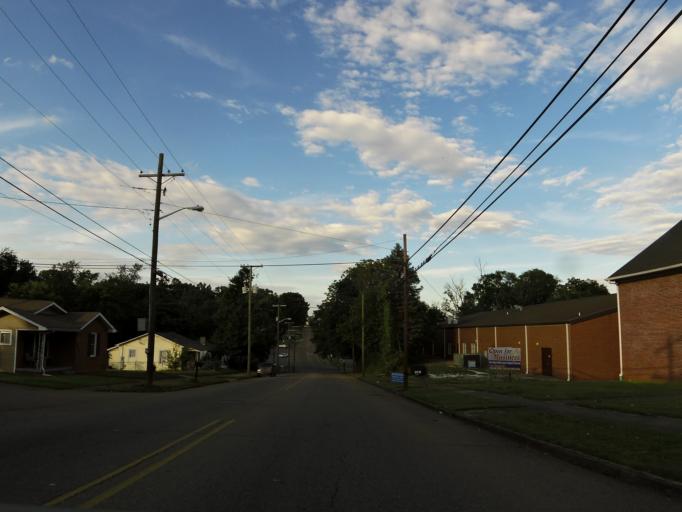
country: US
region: Tennessee
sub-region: Knox County
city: Knoxville
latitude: 35.9963
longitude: -83.9077
